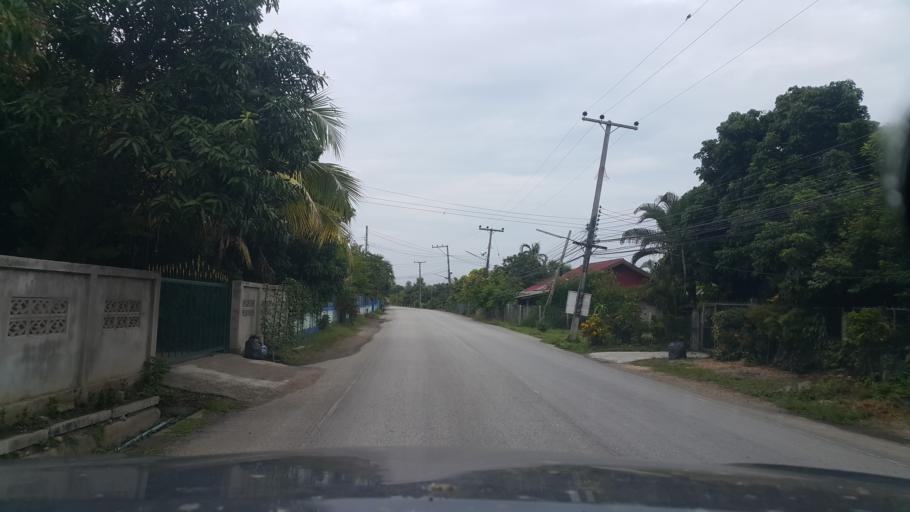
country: TH
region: Chiang Mai
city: San Pa Tong
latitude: 18.6481
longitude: 98.8393
